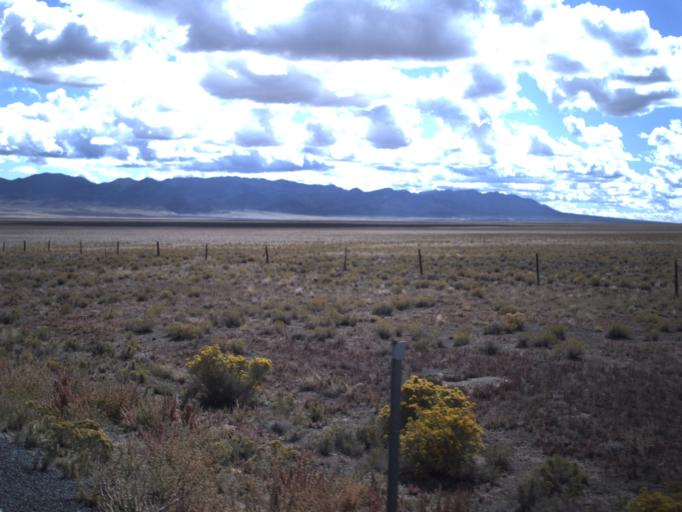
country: US
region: Utah
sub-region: Beaver County
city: Milford
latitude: 38.5541
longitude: -113.7409
